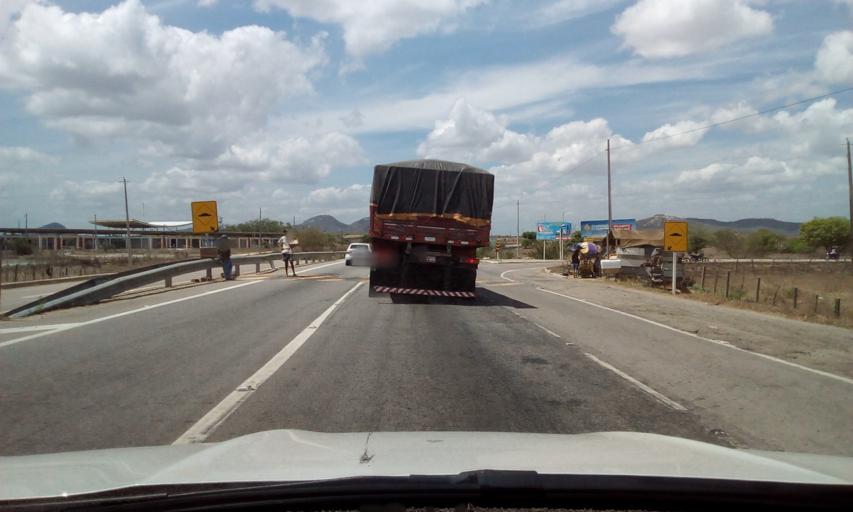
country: BR
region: Paraiba
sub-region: Gurinhem
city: Gurinhem
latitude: -7.1654
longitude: -35.3541
